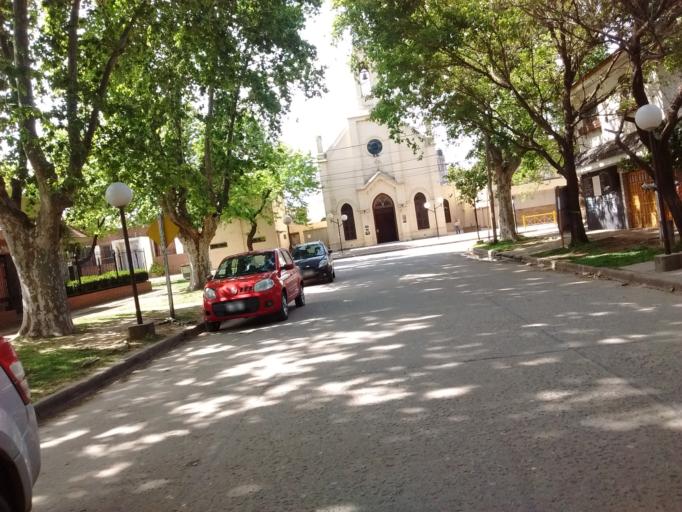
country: AR
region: Santa Fe
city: Funes
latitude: -32.9152
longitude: -60.8100
